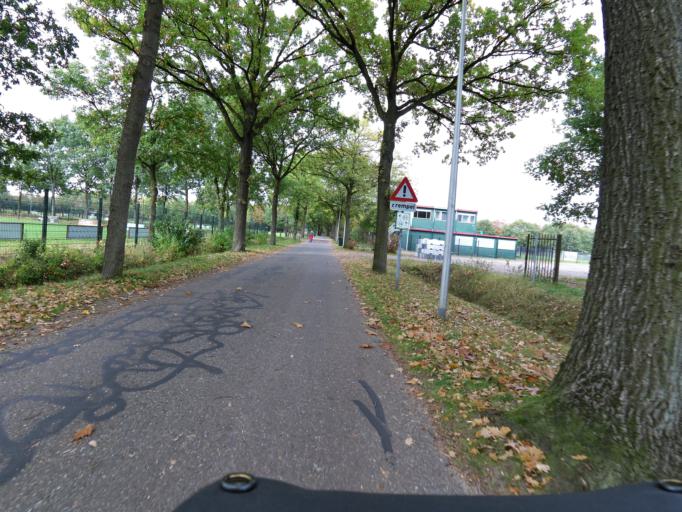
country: BE
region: Flanders
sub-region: Provincie Antwerpen
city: Stabroek
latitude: 51.3691
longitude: 4.3995
